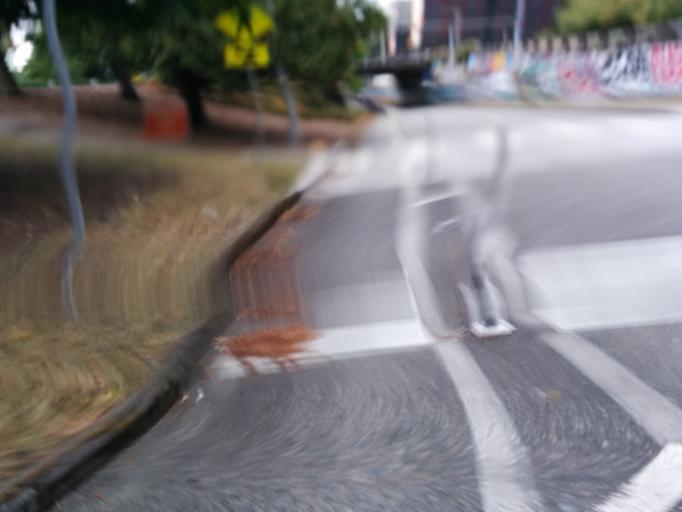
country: US
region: Washington
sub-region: King County
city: Seattle
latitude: 47.6562
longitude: -122.3164
